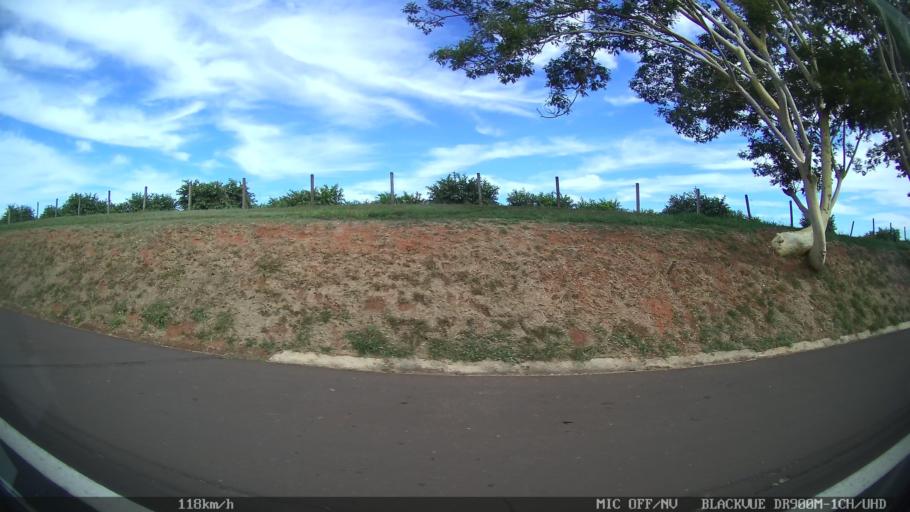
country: BR
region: Sao Paulo
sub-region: Taquaritinga
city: Taquaritinga
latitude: -21.4591
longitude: -48.6227
